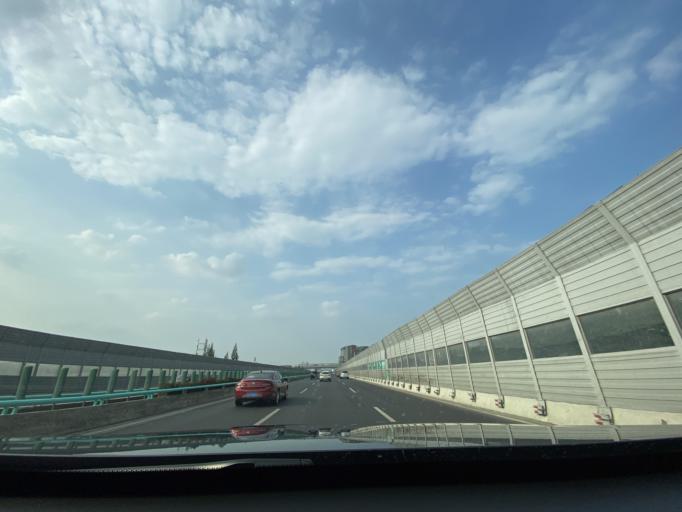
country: CN
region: Sichuan
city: Chengdu
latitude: 30.6115
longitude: 104.0335
